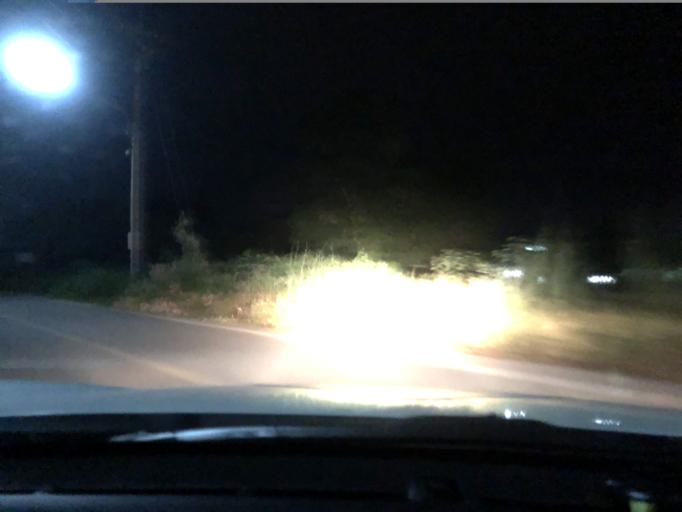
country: TH
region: Nakhon Sawan
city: Takhli
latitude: 15.2592
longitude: 100.3328
